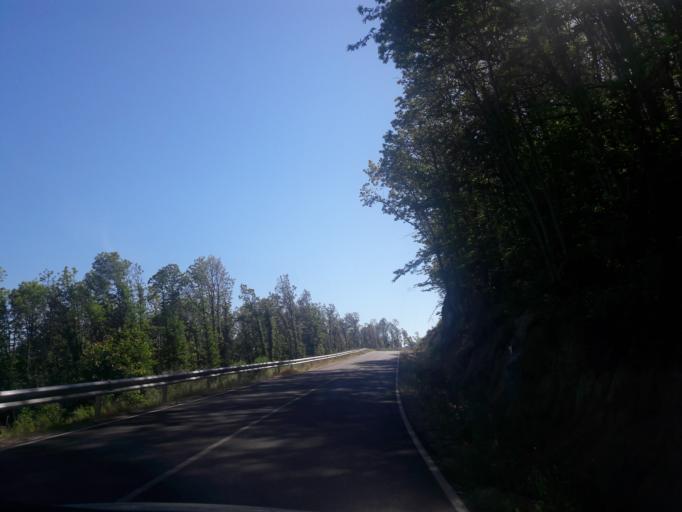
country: ES
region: Castille and Leon
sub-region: Provincia de Salamanca
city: Montemayor del Rio
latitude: 40.3358
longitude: -5.8965
